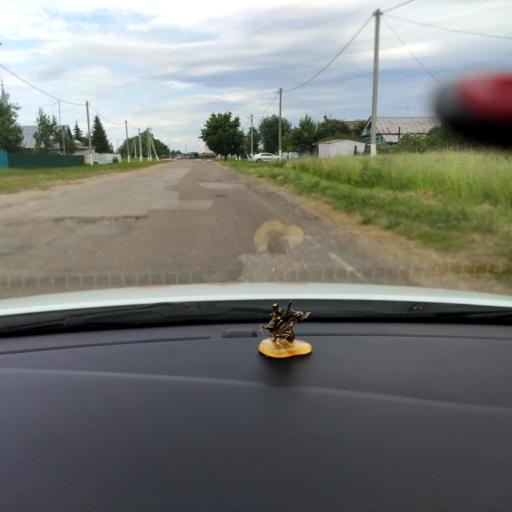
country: RU
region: Tatarstan
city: Kuybyshevskiy Zaton
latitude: 55.2866
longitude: 49.3483
